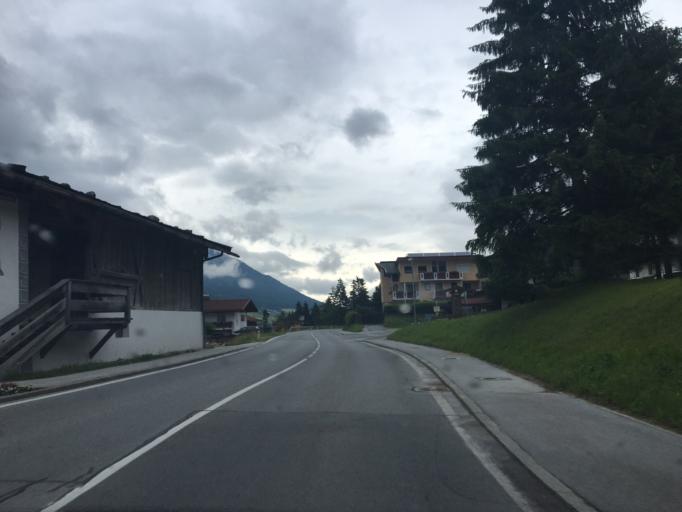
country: AT
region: Tyrol
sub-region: Politischer Bezirk Innsbruck Land
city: Neustift im Stubaital
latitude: 47.1275
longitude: 11.3344
